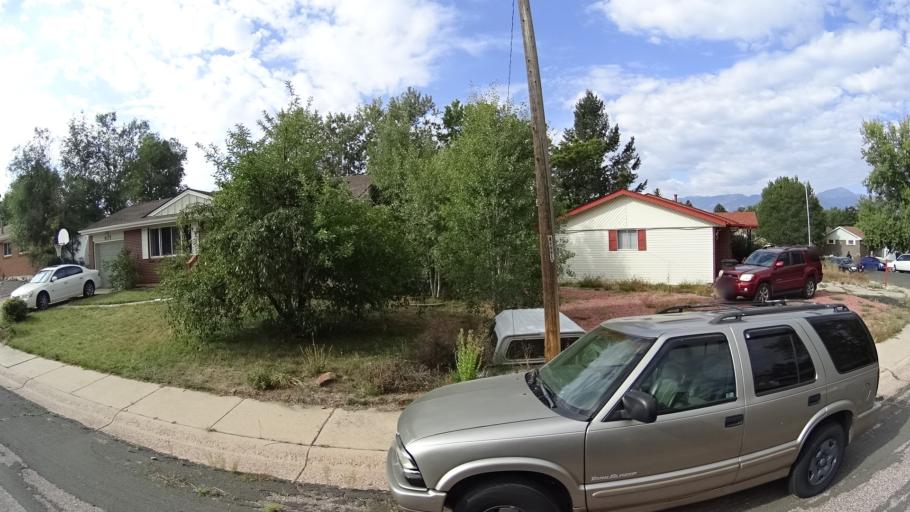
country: US
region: Colorado
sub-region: El Paso County
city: Cimarron Hills
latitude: 38.8454
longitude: -104.7518
